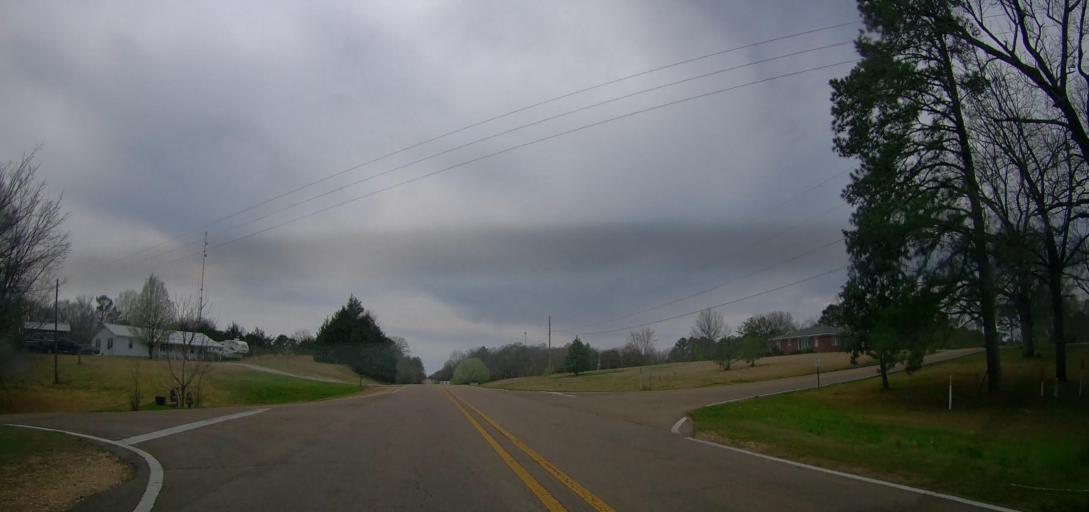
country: US
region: Mississippi
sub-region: Itawamba County
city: Mantachie
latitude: 34.2585
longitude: -88.5097
